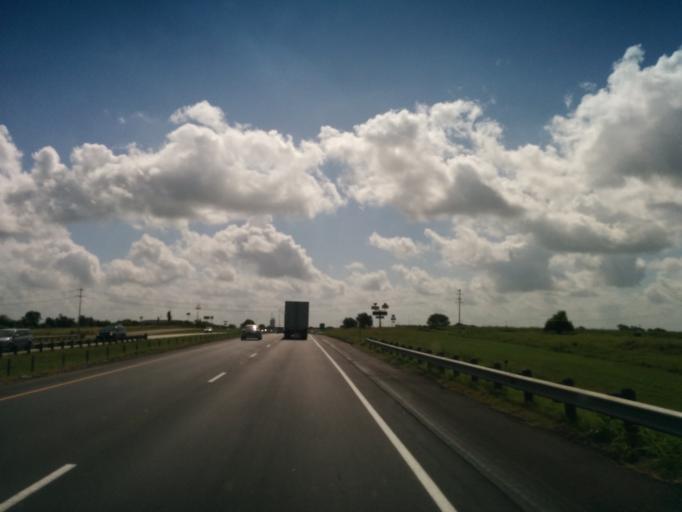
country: US
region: Texas
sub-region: Colorado County
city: Weimar
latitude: 29.6911
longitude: -96.7843
